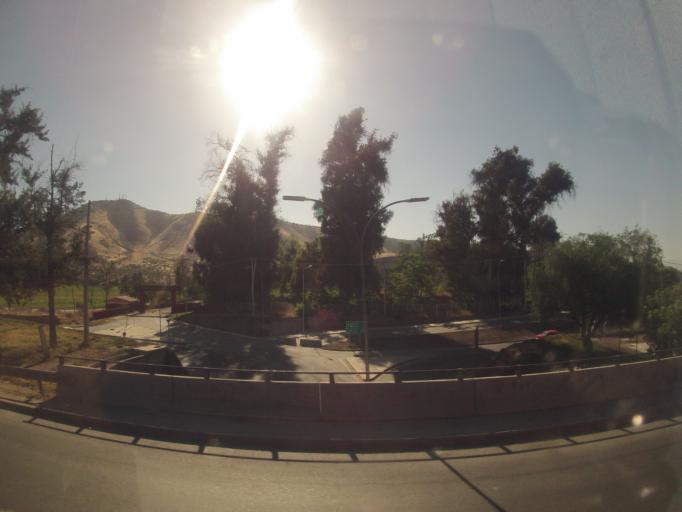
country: CL
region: Santiago Metropolitan
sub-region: Provincia de Maipo
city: San Bernardo
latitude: -33.5880
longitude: -70.7150
